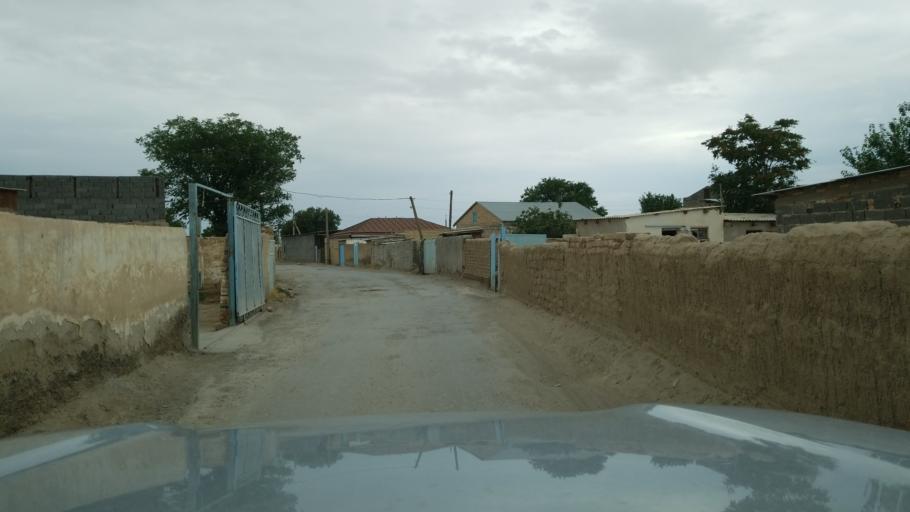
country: TM
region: Balkan
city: Serdar
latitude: 38.9876
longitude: 56.2769
